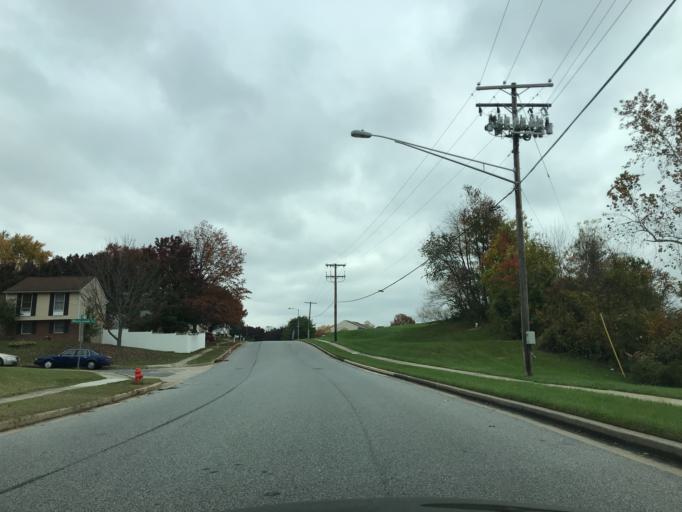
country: US
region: Maryland
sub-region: Baltimore County
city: Carney
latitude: 39.3860
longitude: -76.5155
